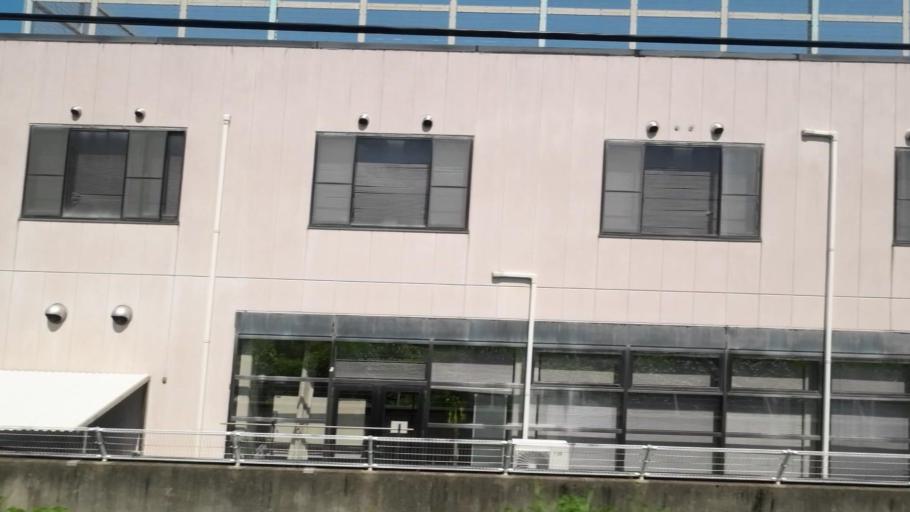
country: JP
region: Ehime
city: Niihama
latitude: 33.9422
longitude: 133.2881
